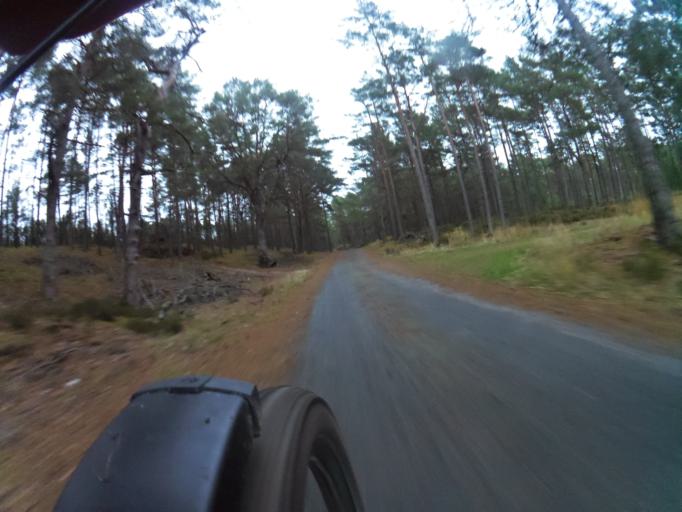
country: PL
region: Pomeranian Voivodeship
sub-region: Powiat wejherowski
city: Choczewo
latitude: 54.7947
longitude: 17.7722
